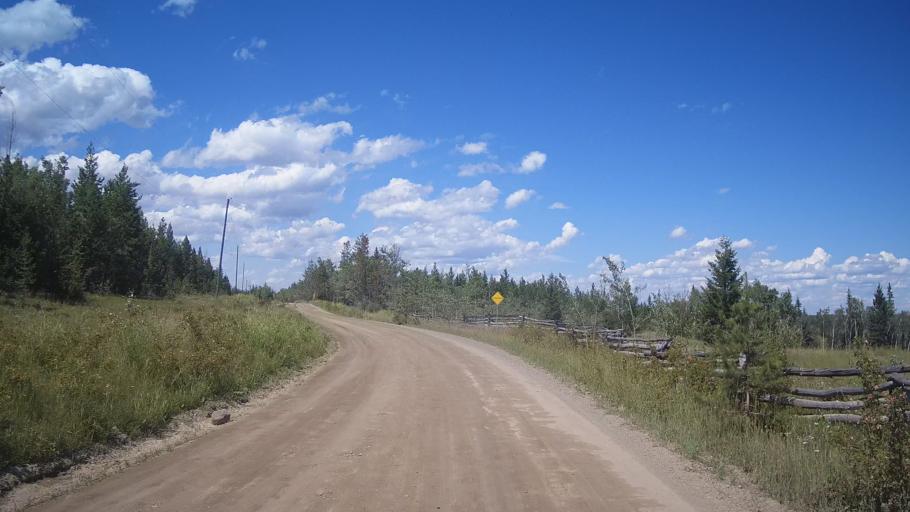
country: CA
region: British Columbia
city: Cache Creek
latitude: 51.2643
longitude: -121.6975
